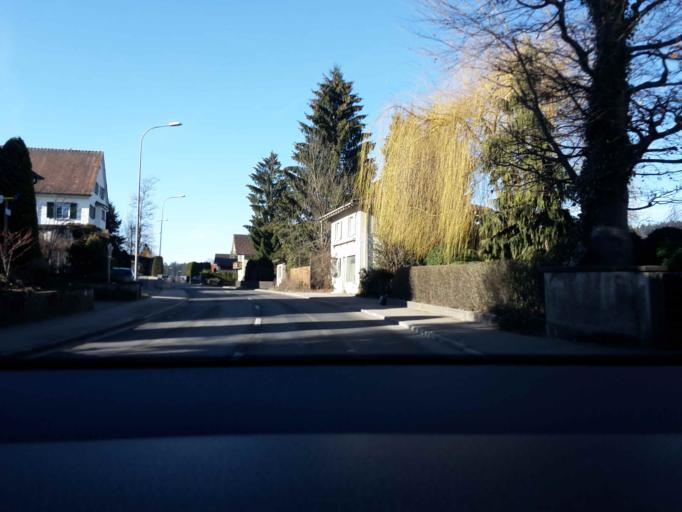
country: CH
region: Bern
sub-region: Oberaargau
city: Huttwil
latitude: 47.1130
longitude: 7.8376
